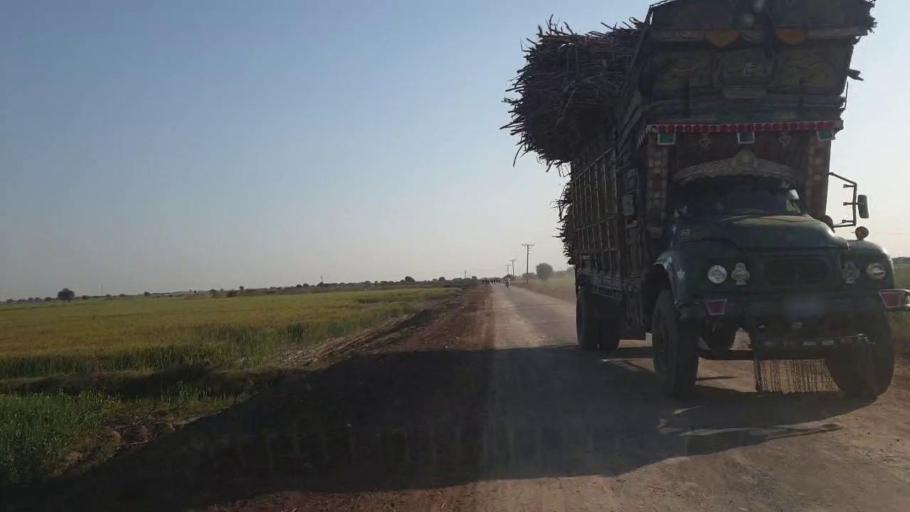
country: PK
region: Sindh
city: Chambar
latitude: 25.2859
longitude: 68.7498
